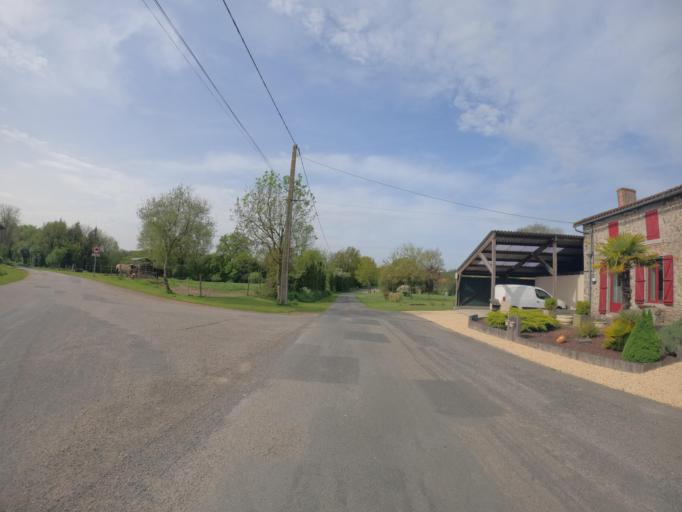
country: FR
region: Poitou-Charentes
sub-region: Departement des Deux-Sevres
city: La Chapelle-Saint-Laurent
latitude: 46.6981
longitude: -0.5233
